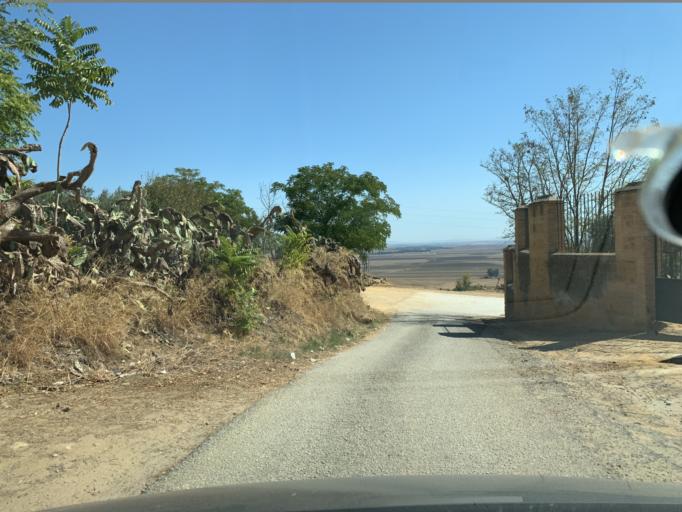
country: ES
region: Andalusia
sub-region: Provincia de Sevilla
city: Carmona
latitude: 37.4706
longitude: -5.6340
